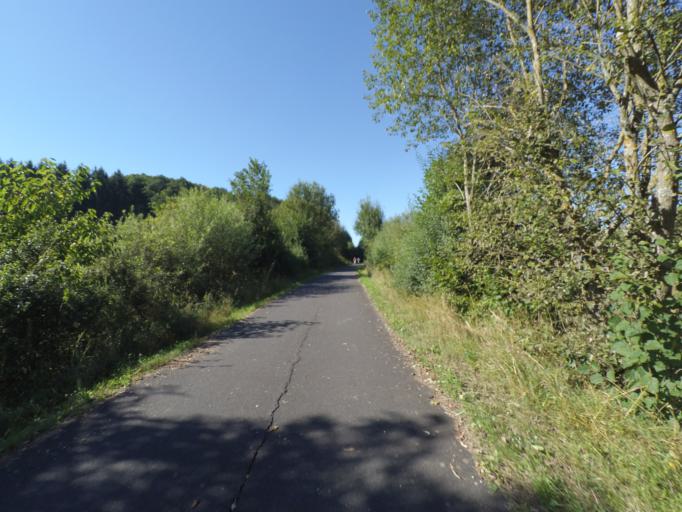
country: DE
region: Rheinland-Pfalz
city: Udler
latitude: 50.1318
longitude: 6.8902
